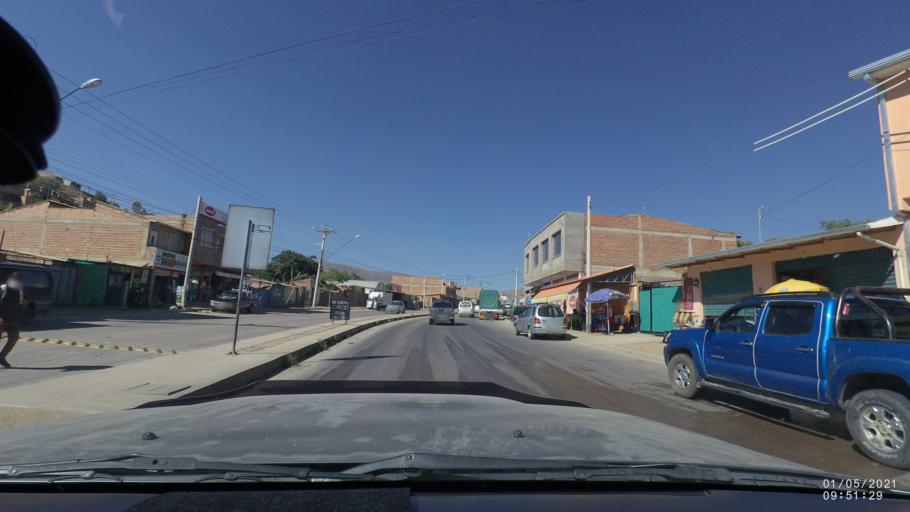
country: BO
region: Cochabamba
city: Cochabamba
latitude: -17.4713
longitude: -66.1710
